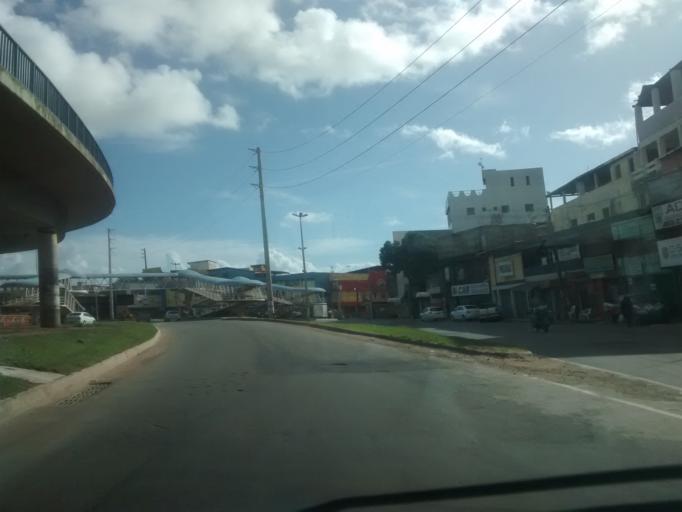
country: BR
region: Bahia
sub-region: Salvador
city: Salvador
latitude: -12.9752
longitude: -38.4593
